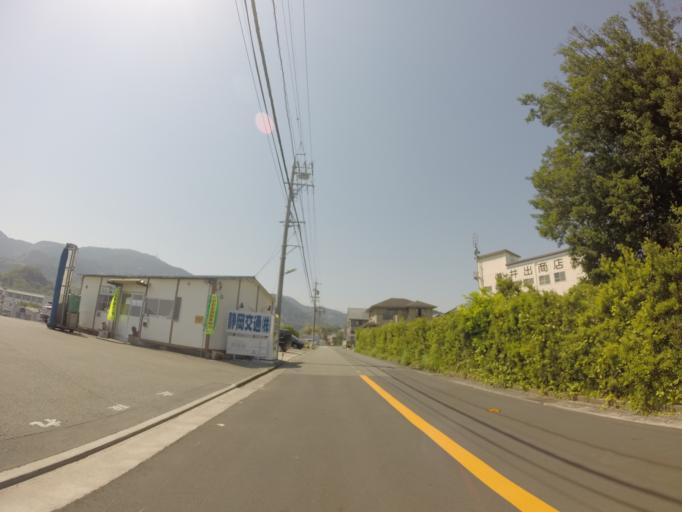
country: JP
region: Shizuoka
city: Fujinomiya
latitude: 35.1101
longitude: 138.5644
